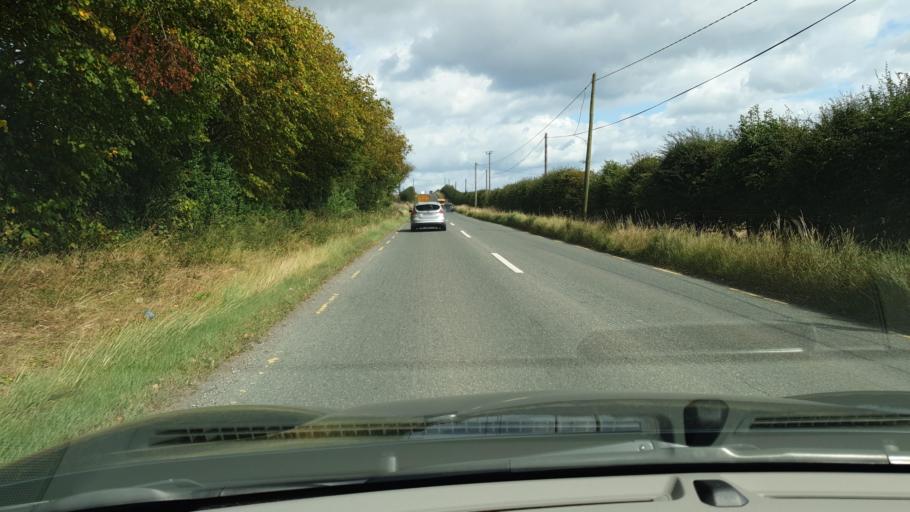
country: IE
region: Leinster
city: Lusk
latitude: 53.5472
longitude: -6.1575
